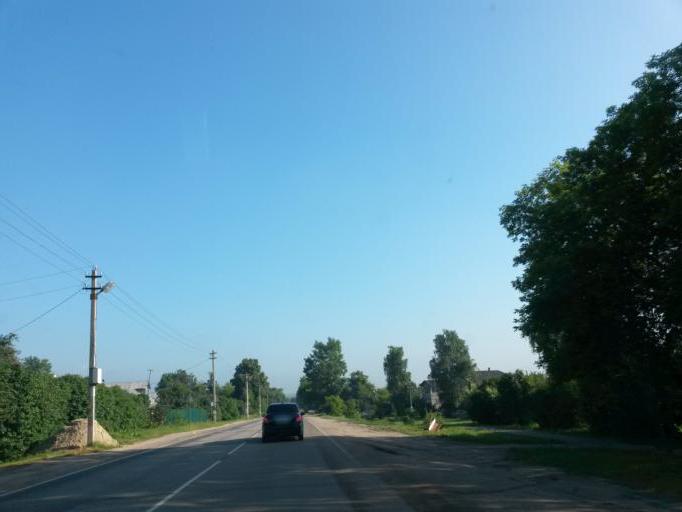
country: RU
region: Moskovskaya
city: Yam
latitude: 55.4784
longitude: 37.7523
